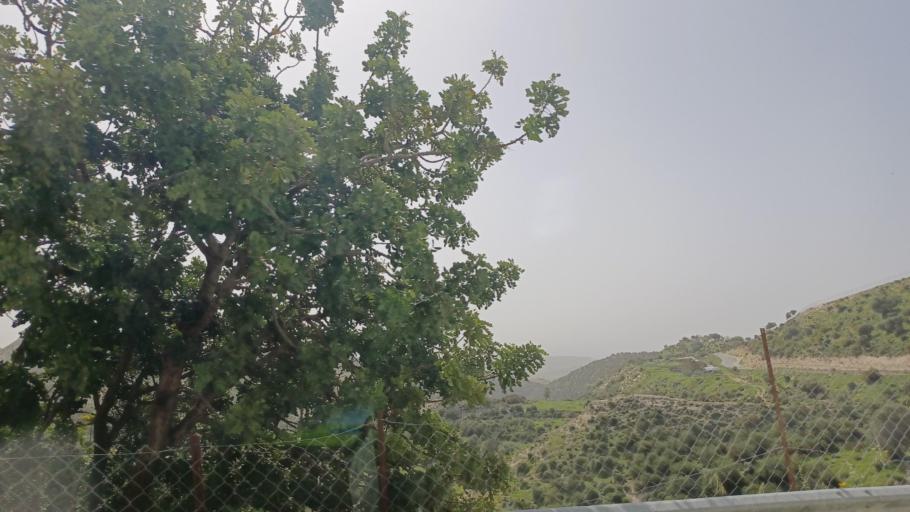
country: CY
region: Limassol
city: Pissouri
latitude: 34.6967
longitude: 32.7057
